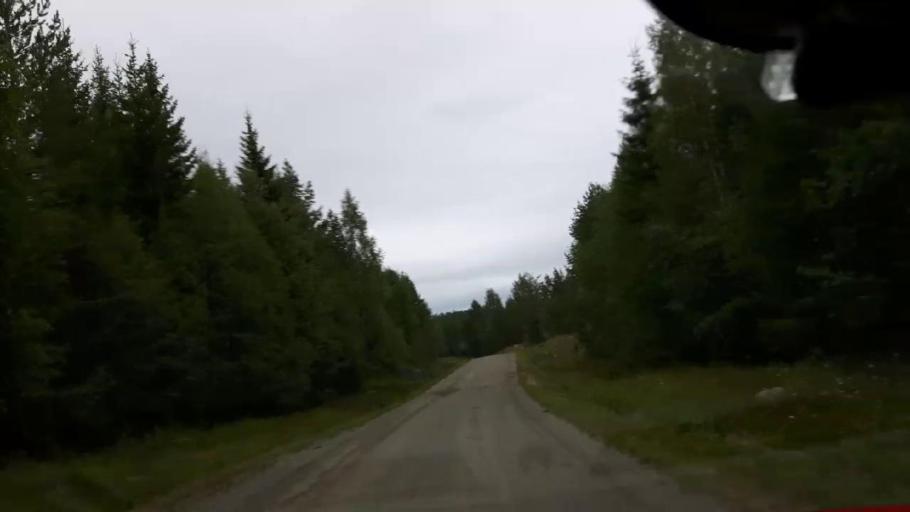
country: SE
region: Vaesternorrland
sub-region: Ange Kommun
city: Fransta
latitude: 62.8567
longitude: 15.9798
